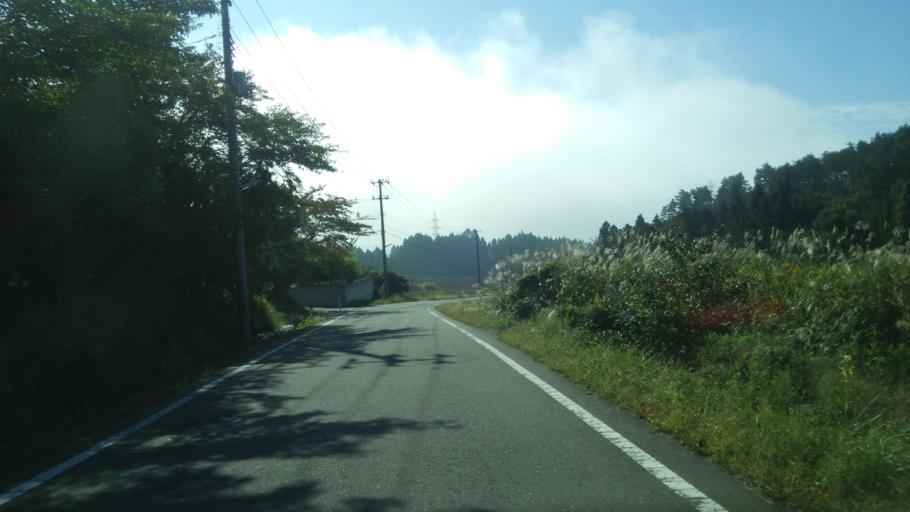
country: JP
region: Fukushima
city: Kitakata
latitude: 37.5866
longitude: 139.9460
